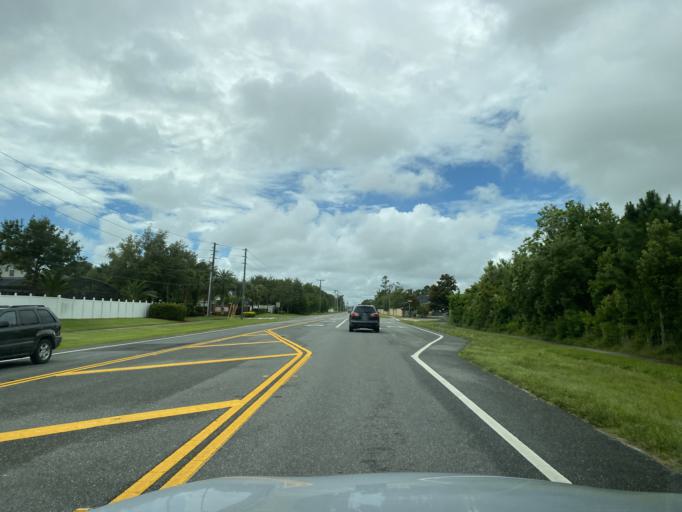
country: US
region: Florida
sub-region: Brevard County
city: West Melbourne
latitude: 28.0564
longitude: -80.6540
